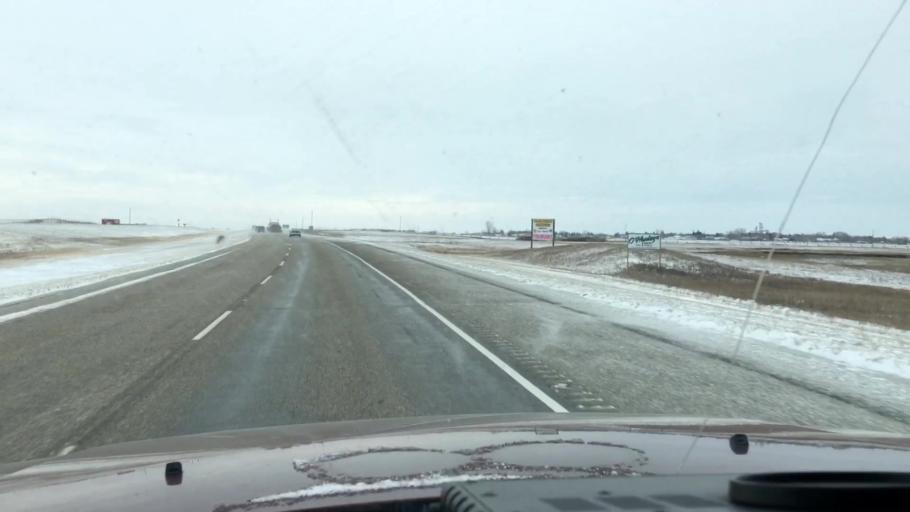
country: CA
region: Saskatchewan
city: Saskatoon
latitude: 51.6456
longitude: -106.4379
